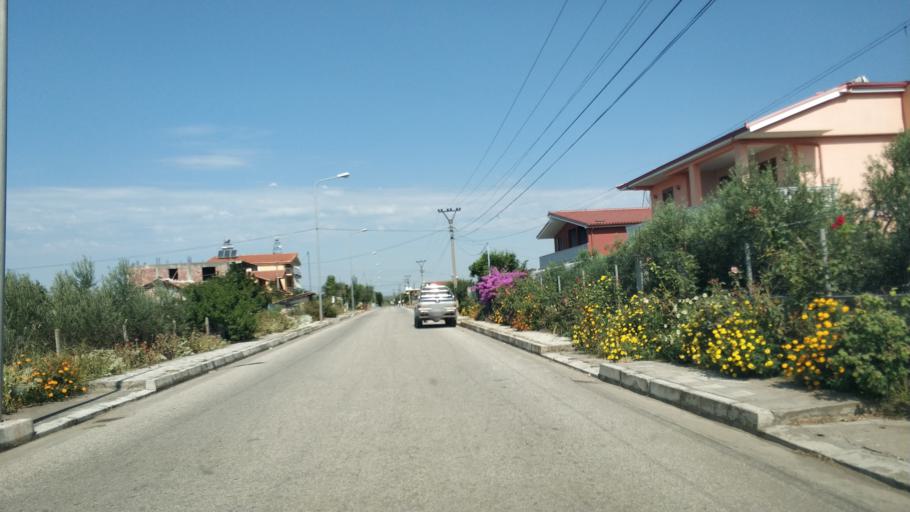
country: AL
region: Fier
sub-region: Rrethi i Lushnjes
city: Divjake
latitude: 40.9997
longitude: 19.5253
